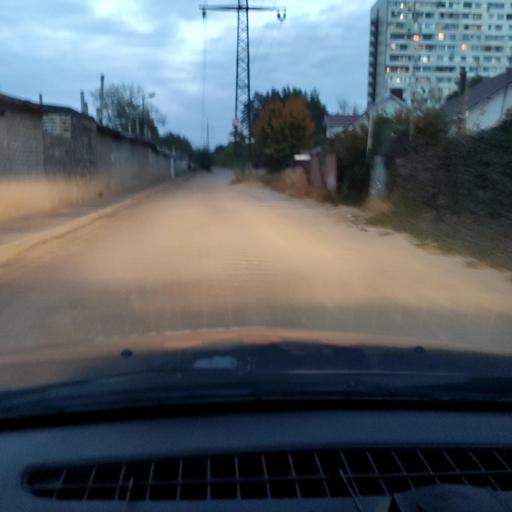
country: RU
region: Voronezj
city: Pridonskoy
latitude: 51.6884
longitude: 39.0783
